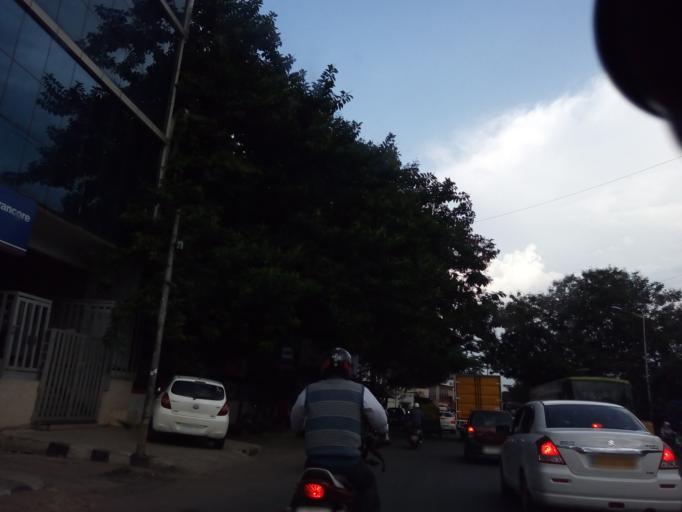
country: IN
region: Karnataka
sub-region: Bangalore Urban
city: Bangalore
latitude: 13.0071
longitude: 77.5925
